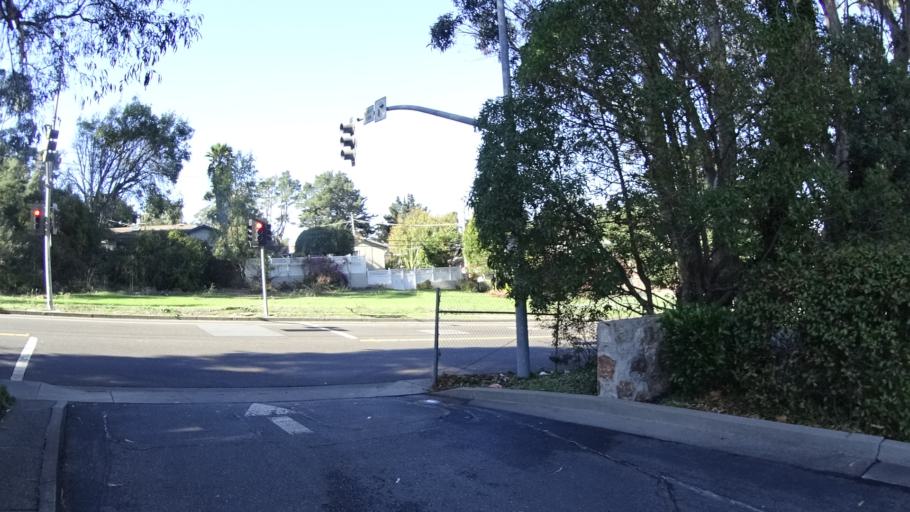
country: US
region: California
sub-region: San Mateo County
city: San Bruno
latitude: 37.6289
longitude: -122.4384
